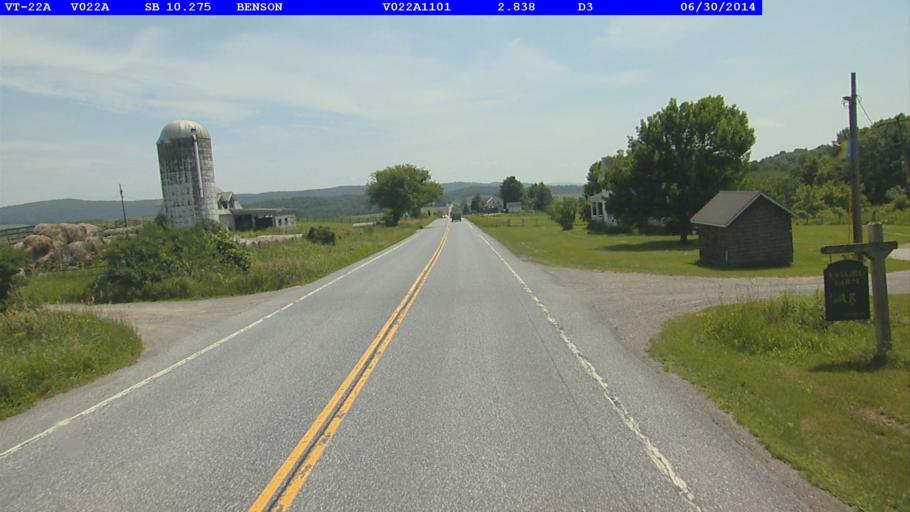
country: US
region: Vermont
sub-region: Rutland County
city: Fair Haven
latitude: 43.7092
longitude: -73.2973
